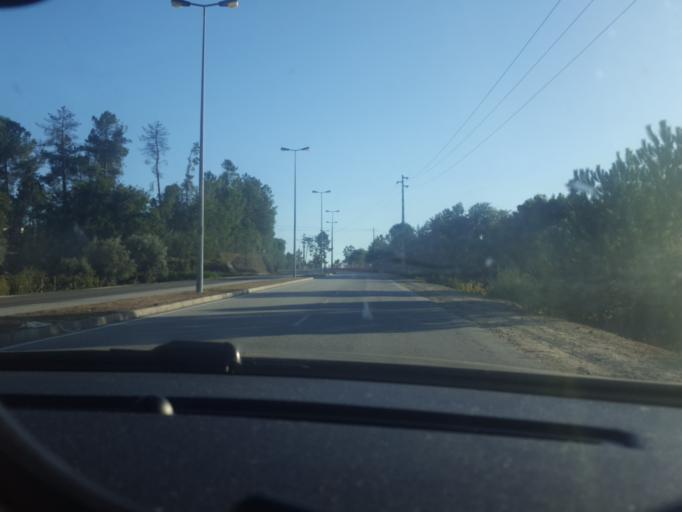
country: PT
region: Viseu
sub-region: Nelas
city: Nelas
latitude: 40.5309
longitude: -7.8651
